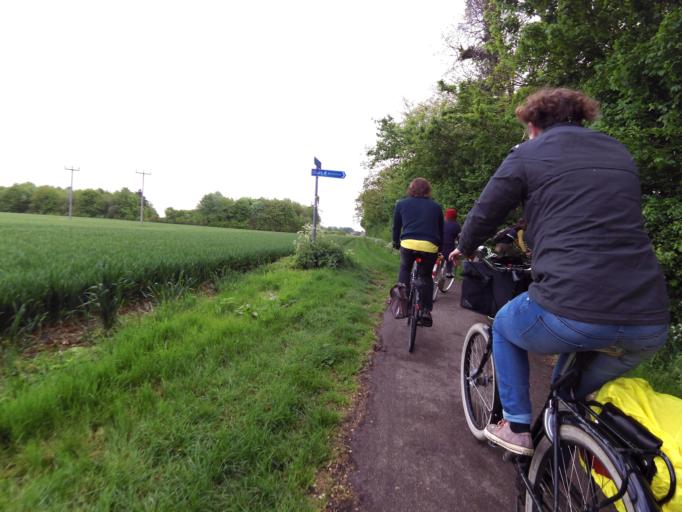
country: GB
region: England
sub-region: Cambridgeshire
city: Fulbourn
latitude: 52.2145
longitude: 0.1829
